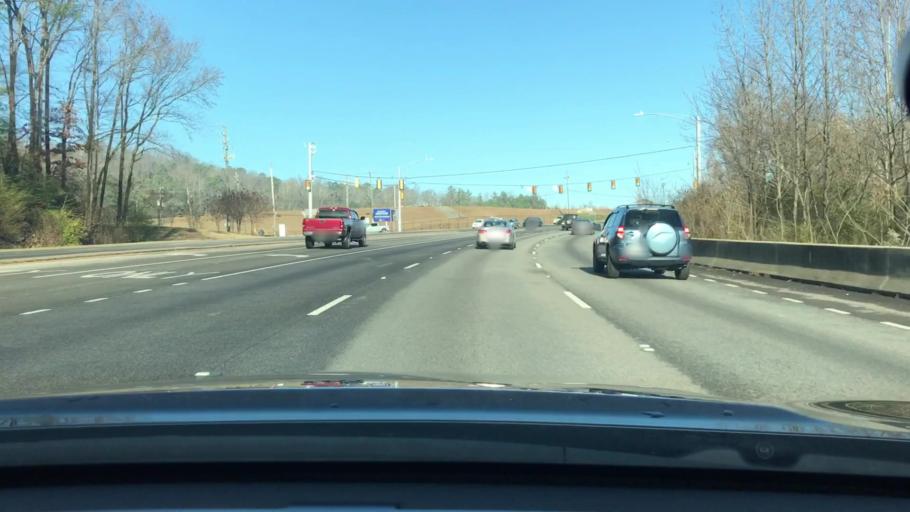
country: US
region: Alabama
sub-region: Jefferson County
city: Cahaba Heights
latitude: 33.4615
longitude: -86.7561
